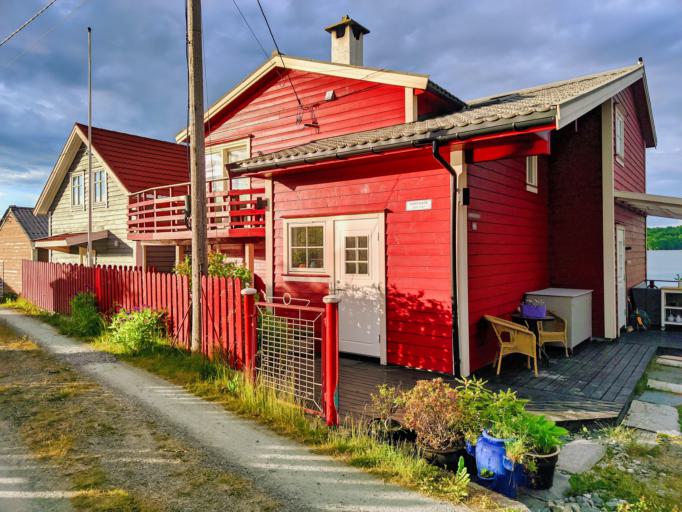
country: NO
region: Hordaland
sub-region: Tysnes
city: Uggdal
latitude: 60.0439
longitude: 5.5282
